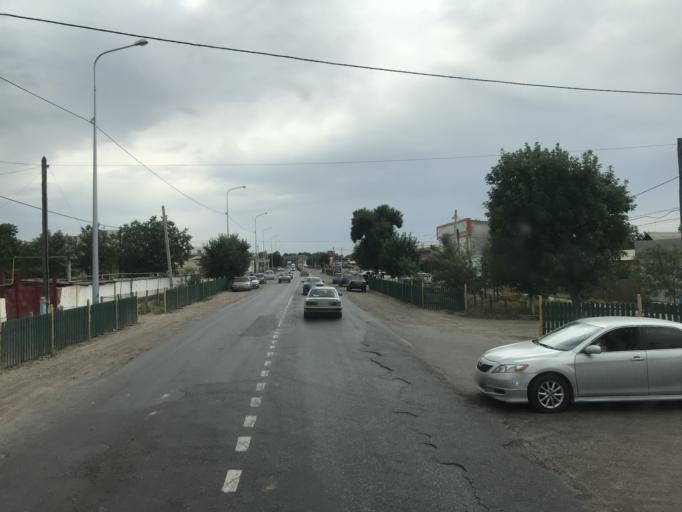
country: KZ
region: Ongtustik Qazaqstan
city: Saryaghash
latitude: 41.3468
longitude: 68.9593
